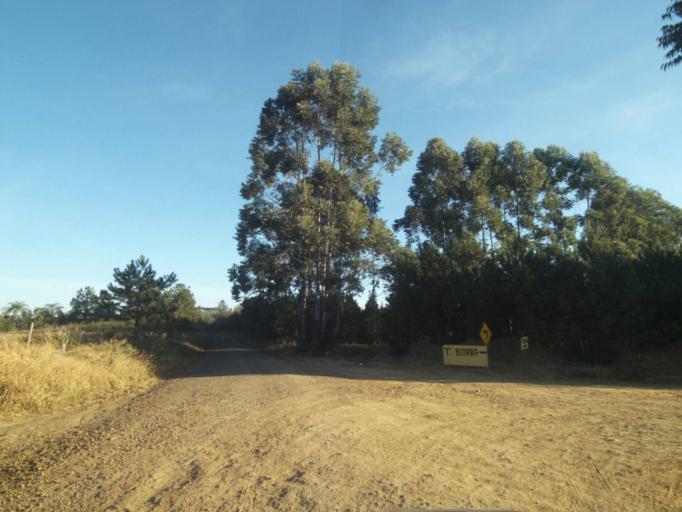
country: BR
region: Parana
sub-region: Telemaco Borba
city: Telemaco Borba
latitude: -24.4278
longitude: -50.5969
